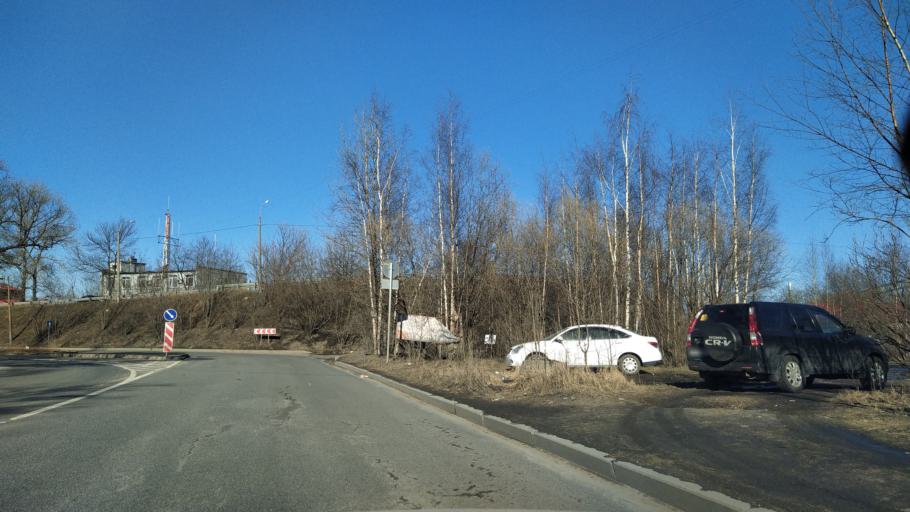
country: RU
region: St.-Petersburg
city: Centralniy
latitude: 59.9034
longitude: 30.3753
